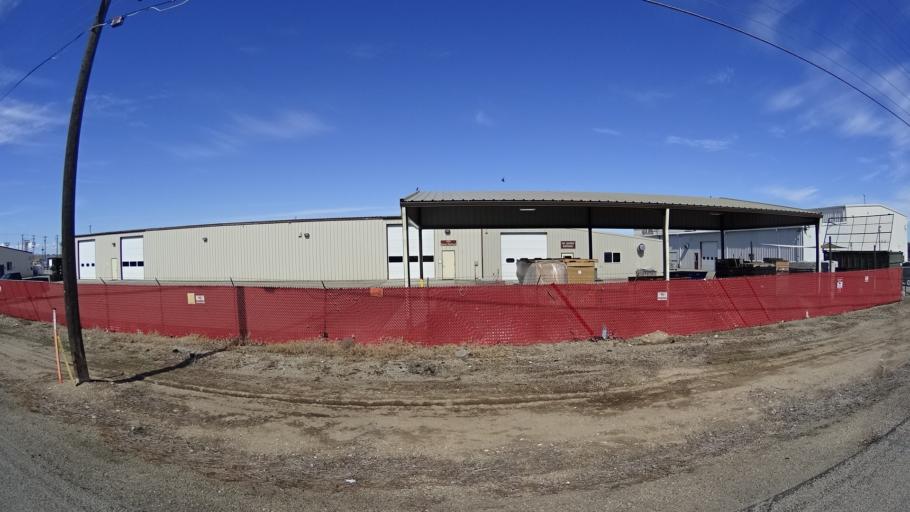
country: US
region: Idaho
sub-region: Ada County
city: Boise
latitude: 43.5655
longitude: -116.2075
